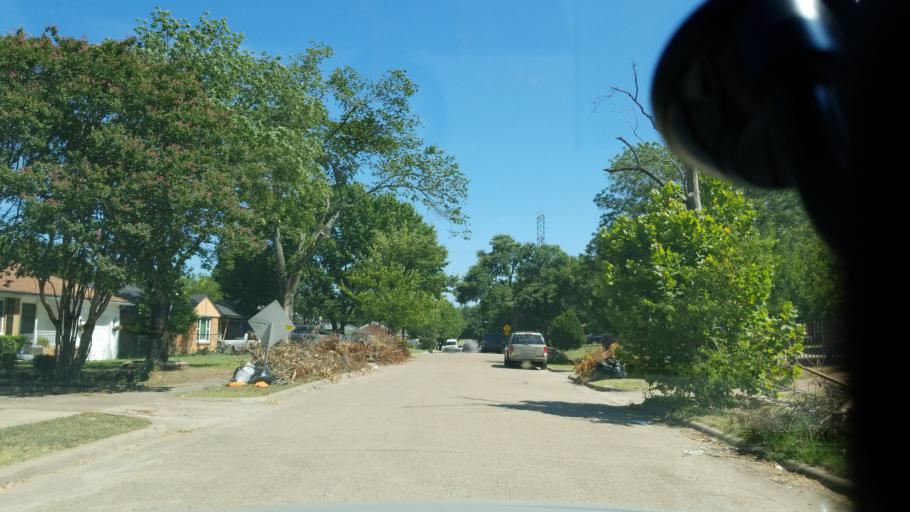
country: US
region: Texas
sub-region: Dallas County
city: Cockrell Hill
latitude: 32.7008
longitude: -96.8172
